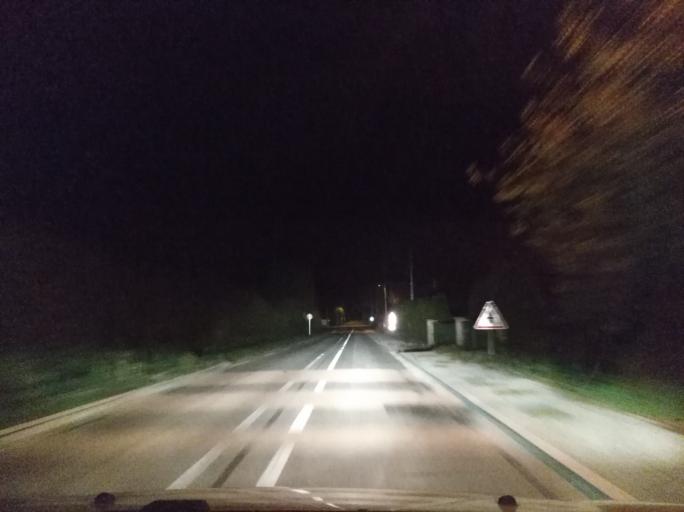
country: FR
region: Franche-Comte
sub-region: Departement du Jura
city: Orgelet
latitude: 46.5260
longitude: 5.5636
